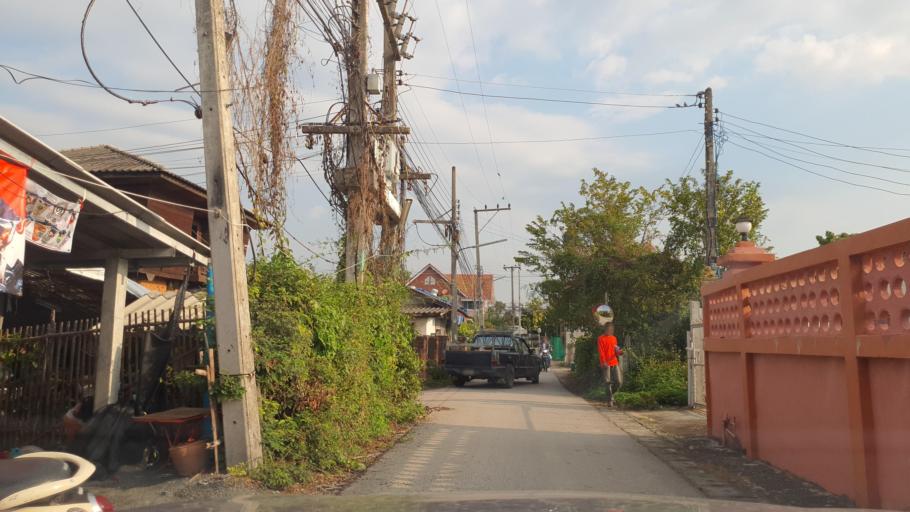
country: TH
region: Chiang Mai
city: San Kamphaeng
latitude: 18.7366
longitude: 99.1086
